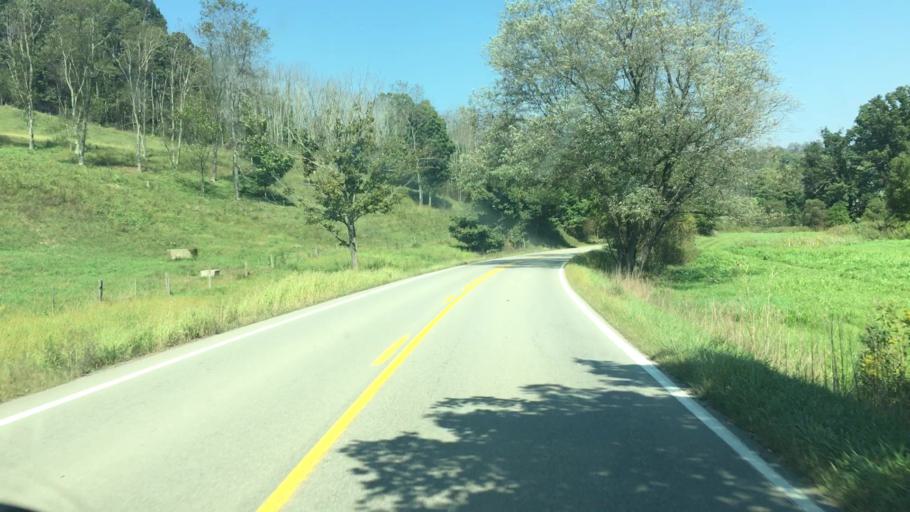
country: US
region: Pennsylvania
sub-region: Washington County
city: Washington
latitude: 40.0214
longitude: -80.3268
